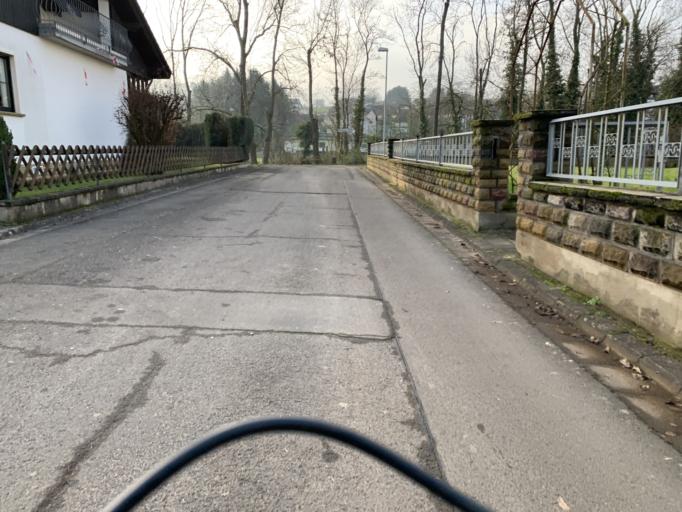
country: DE
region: Rheinland-Pfalz
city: Windesheim
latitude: 49.9089
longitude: 7.8104
